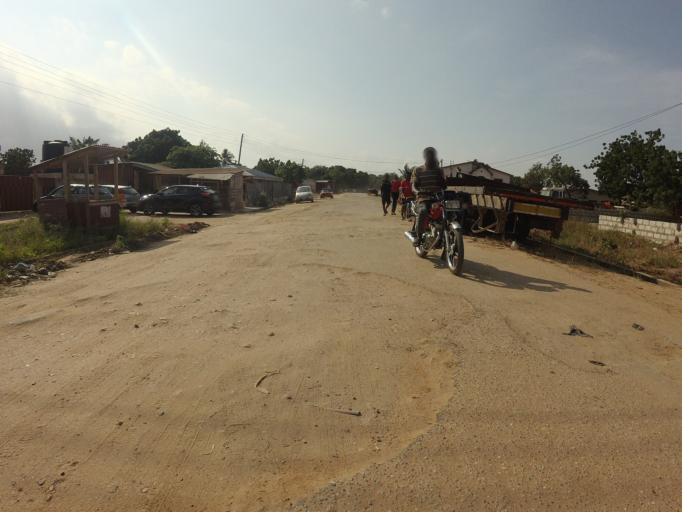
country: GH
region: Greater Accra
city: Dome
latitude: 5.6518
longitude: -0.2630
